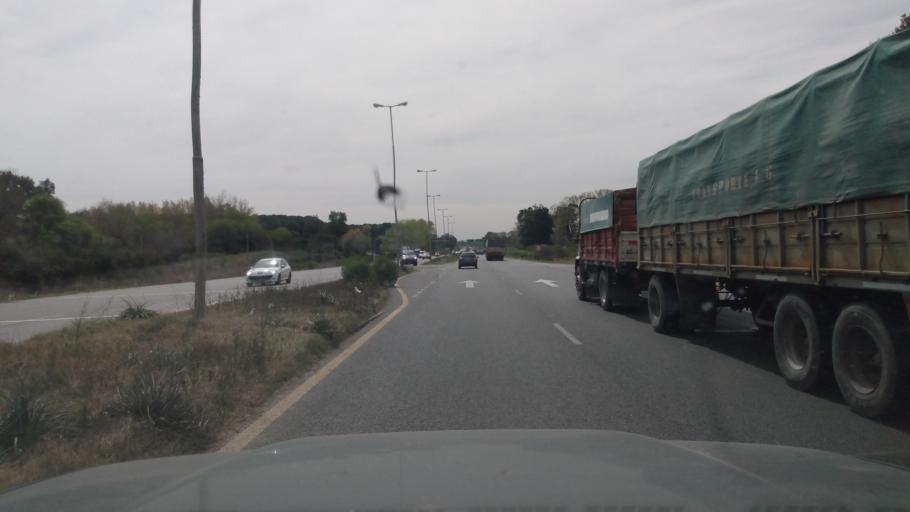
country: AR
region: Buenos Aires
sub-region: Partido de Lujan
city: Lujan
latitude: -34.4674
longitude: -59.0660
